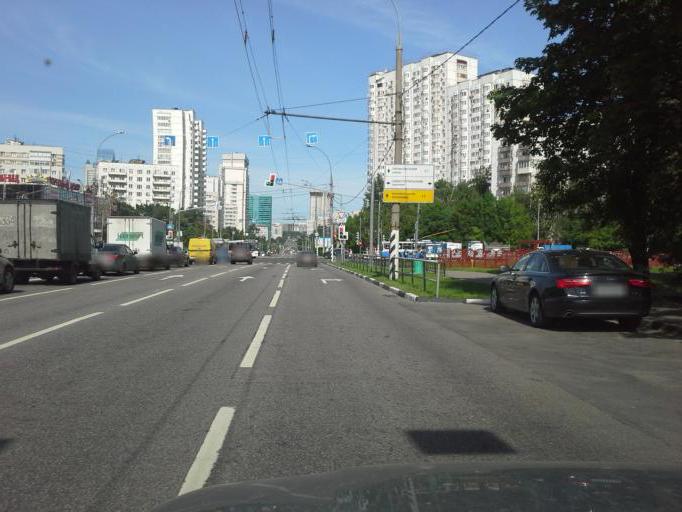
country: RU
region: Moscow
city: Zyuzino
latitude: 55.6562
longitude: 37.5724
